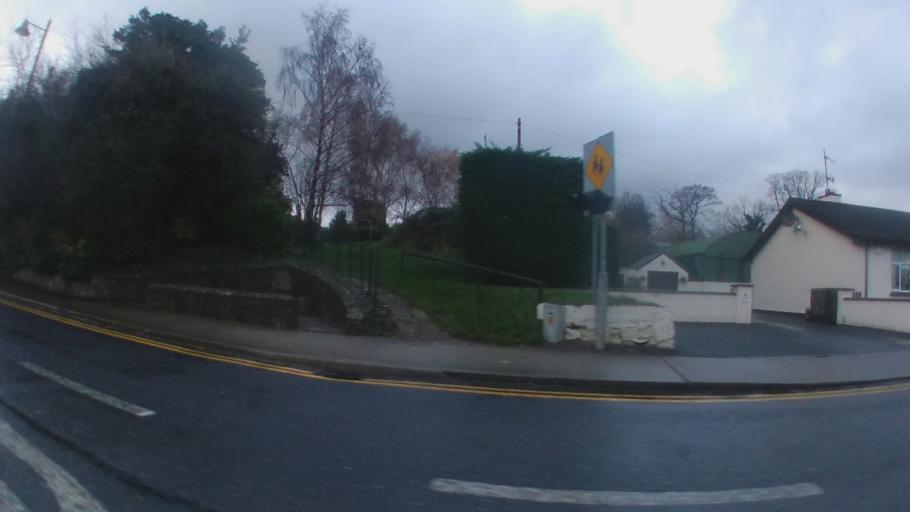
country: IE
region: Leinster
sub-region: Wicklow
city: Kilcoole
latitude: 53.1104
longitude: -6.0654
